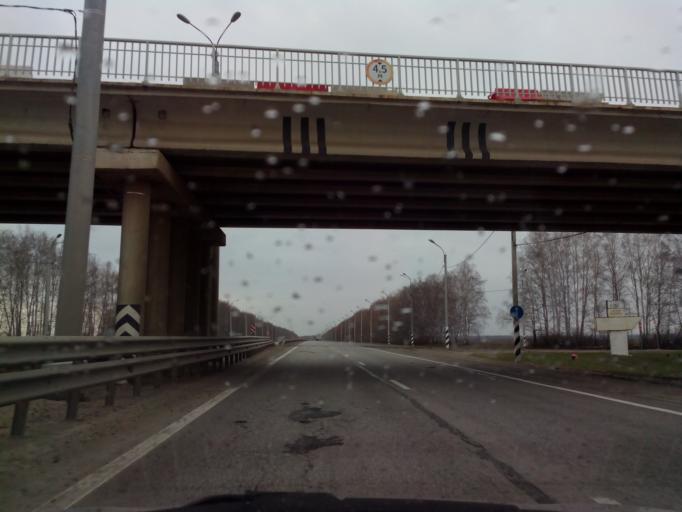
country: RU
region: Tambov
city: Selezni
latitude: 52.7601
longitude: 41.1353
